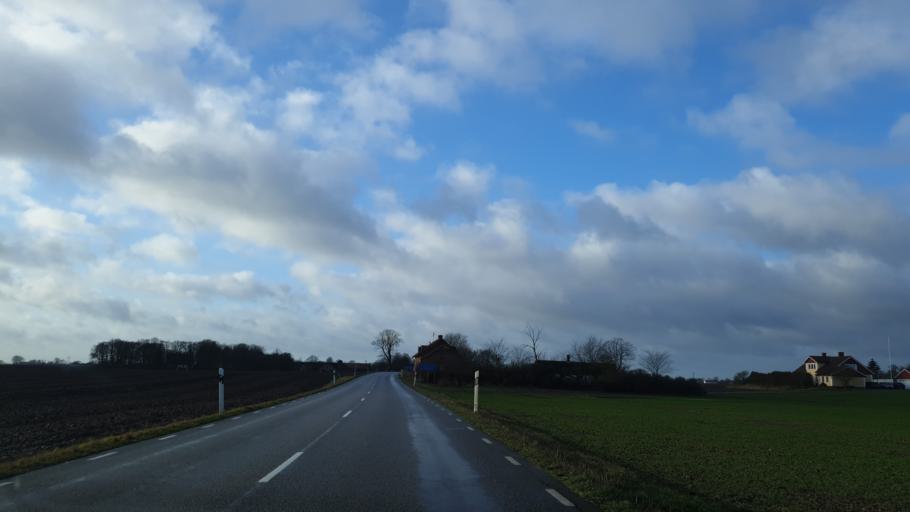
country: SE
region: Skane
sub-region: Trelleborgs Kommun
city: Anderslov
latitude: 55.4229
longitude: 13.4025
